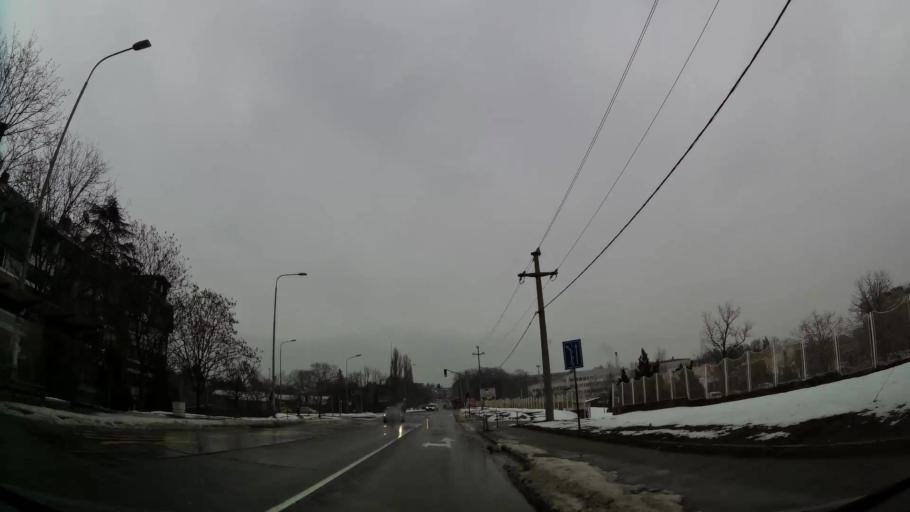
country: RS
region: Central Serbia
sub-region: Belgrade
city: Vozdovac
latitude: 44.7486
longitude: 20.4954
